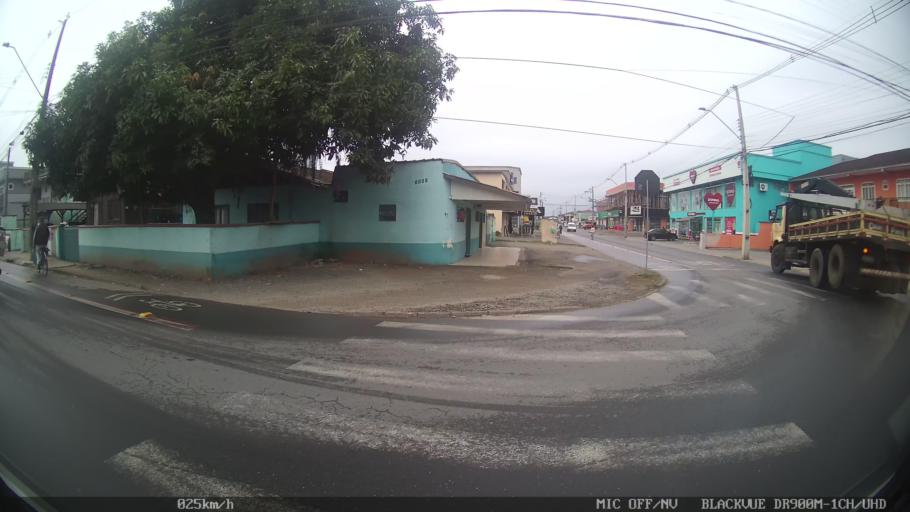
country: BR
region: Santa Catarina
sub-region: Joinville
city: Joinville
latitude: -26.2448
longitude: -48.8119
